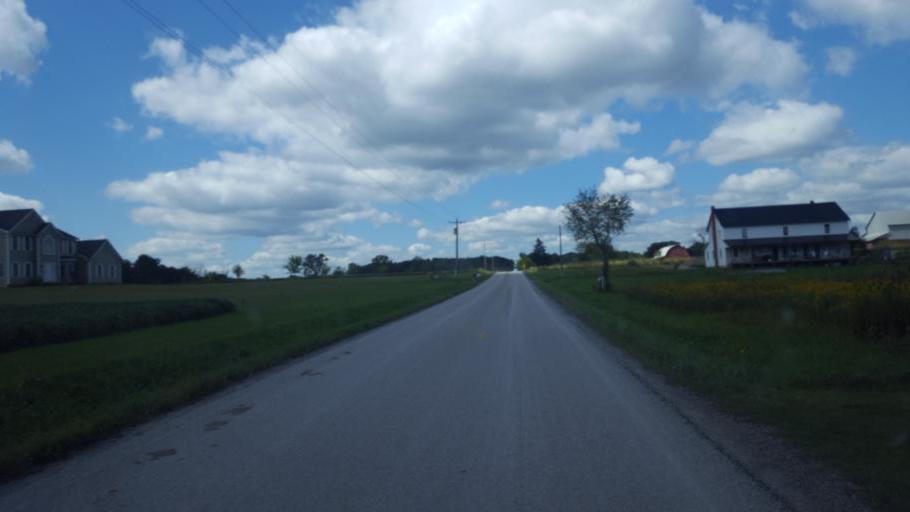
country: US
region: Ohio
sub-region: Wayne County
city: West Salem
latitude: 40.9920
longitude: -82.1589
